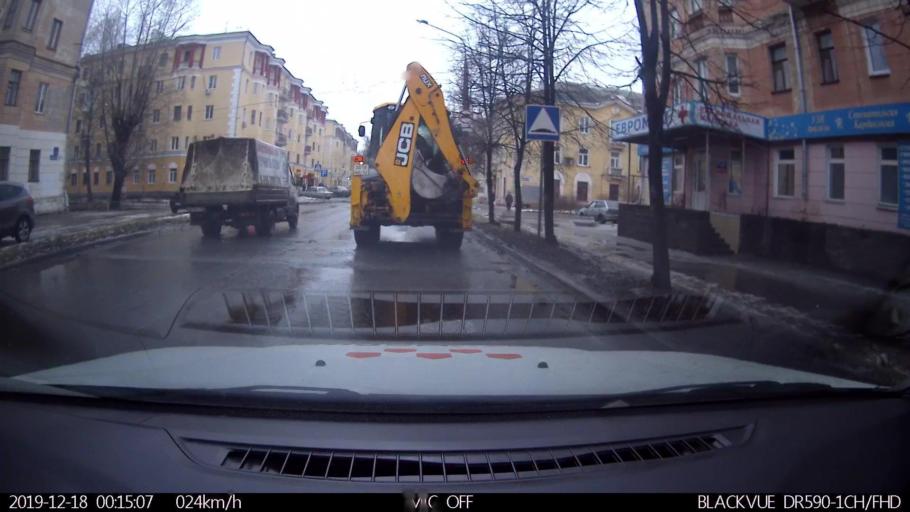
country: RU
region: Nizjnij Novgorod
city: Nizhniy Novgorod
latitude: 56.3334
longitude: 43.8806
